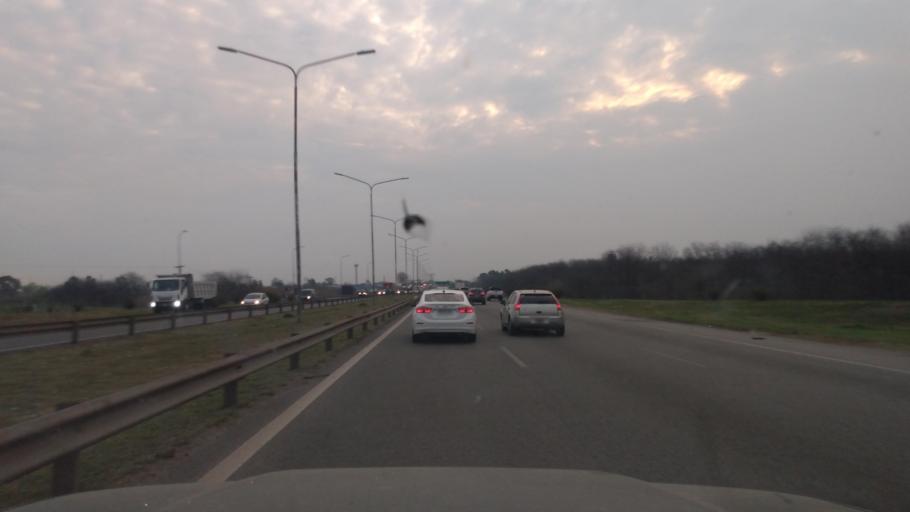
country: AR
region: Buenos Aires
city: Hurlingham
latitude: -34.5669
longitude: -58.6406
